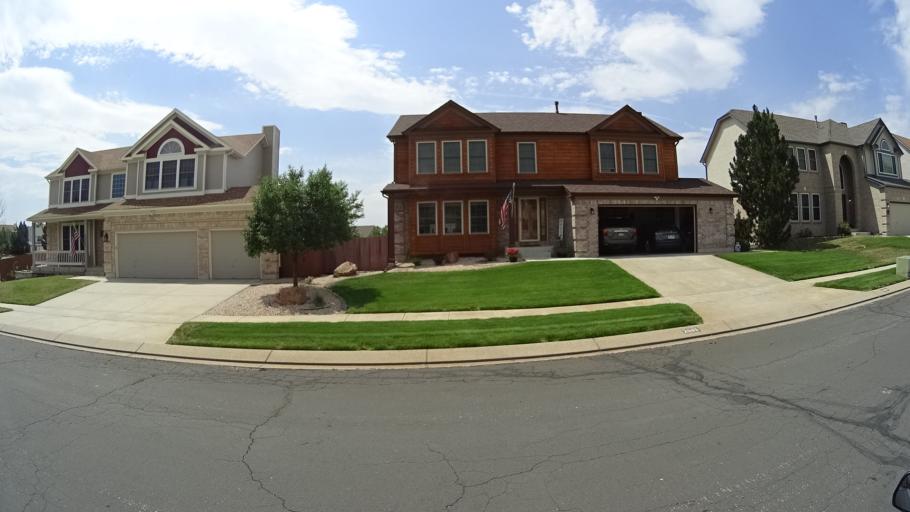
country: US
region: Colorado
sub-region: El Paso County
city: Air Force Academy
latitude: 38.9617
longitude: -104.7776
